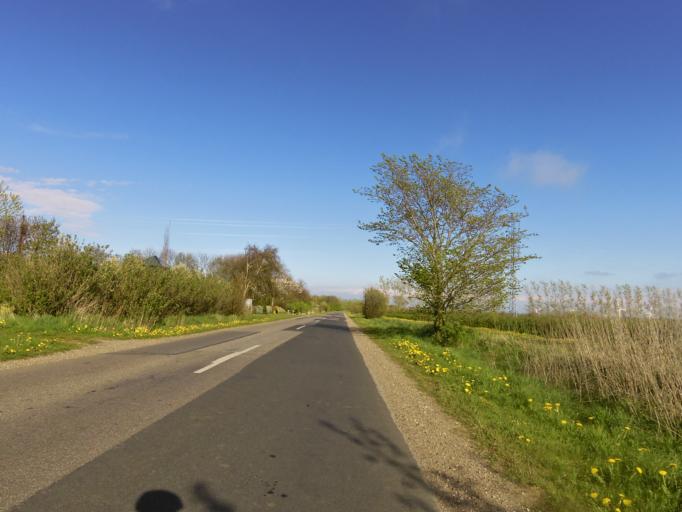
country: DK
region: South Denmark
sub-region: Tonder Kommune
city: Sherrebek
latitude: 55.1552
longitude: 8.8353
